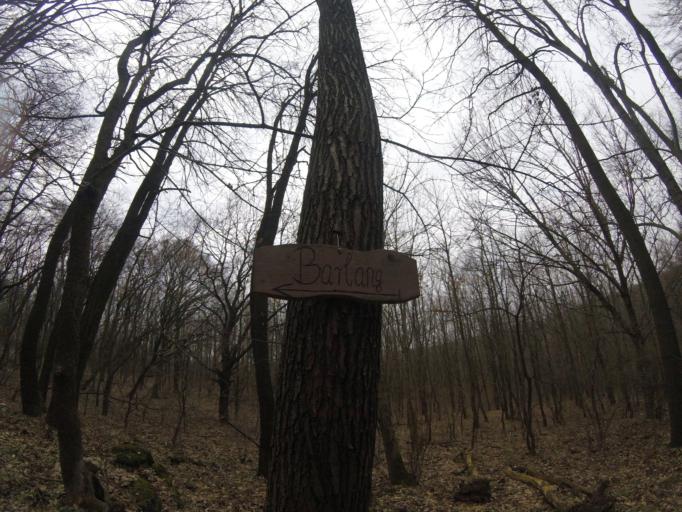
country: HU
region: Komarom-Esztergom
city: Piliscsev
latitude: 47.6880
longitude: 18.8413
